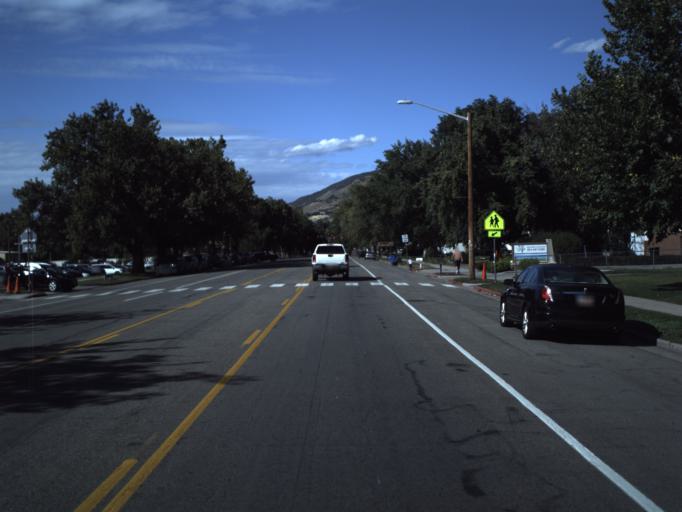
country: US
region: Utah
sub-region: Davis County
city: Farmington
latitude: 40.9775
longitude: -111.8919
